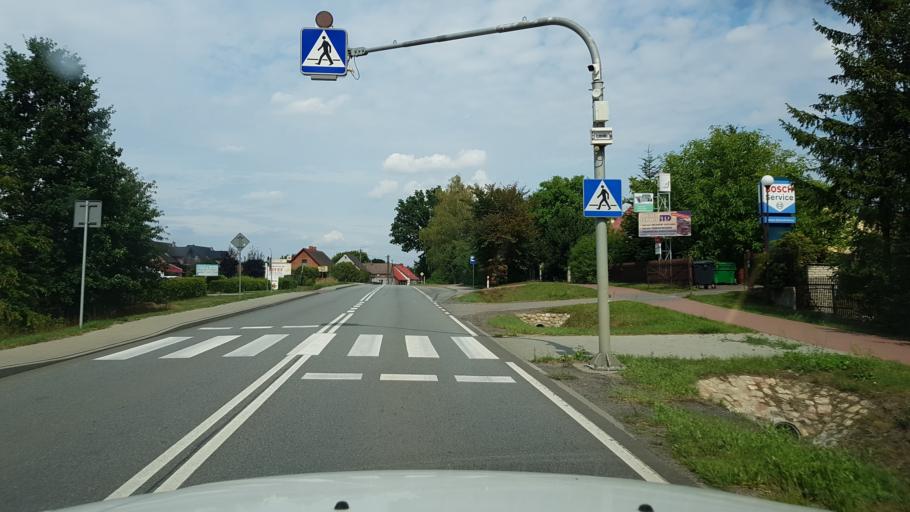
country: PL
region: West Pomeranian Voivodeship
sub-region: Powiat walecki
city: Walcz
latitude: 53.2982
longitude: 16.5279
